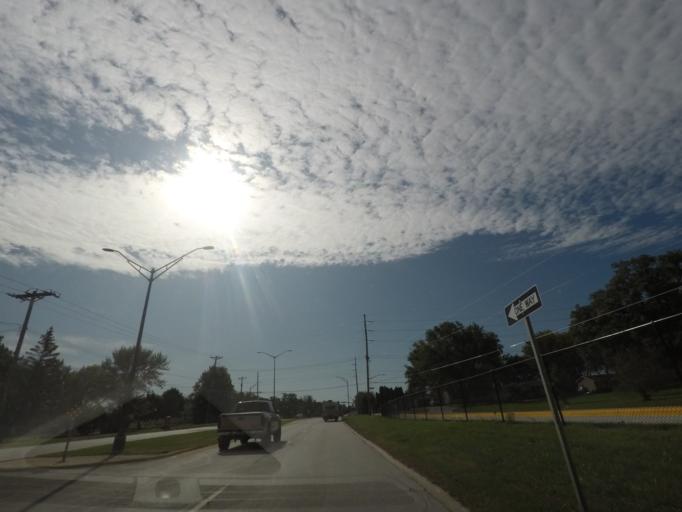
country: US
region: Iowa
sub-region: Story County
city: Ames
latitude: 42.0576
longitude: -93.6209
